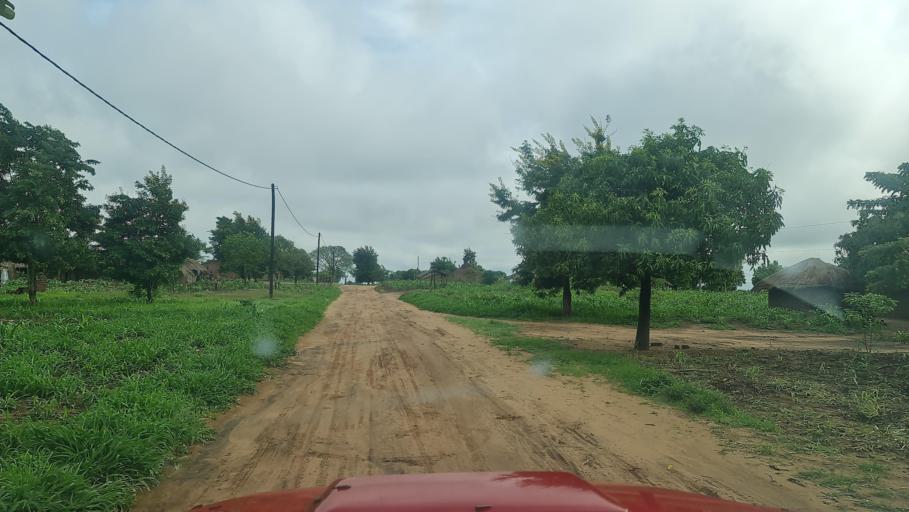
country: MW
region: Southern Region
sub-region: Nsanje District
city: Nsanje
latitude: -17.2186
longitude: 35.6743
